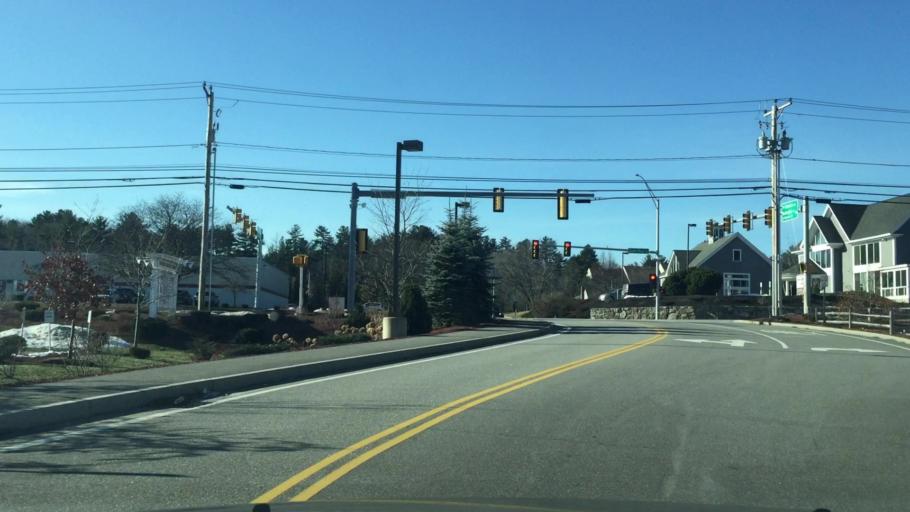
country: US
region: New Hampshire
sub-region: Hillsborough County
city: Bedford
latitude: 42.9611
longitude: -71.4789
